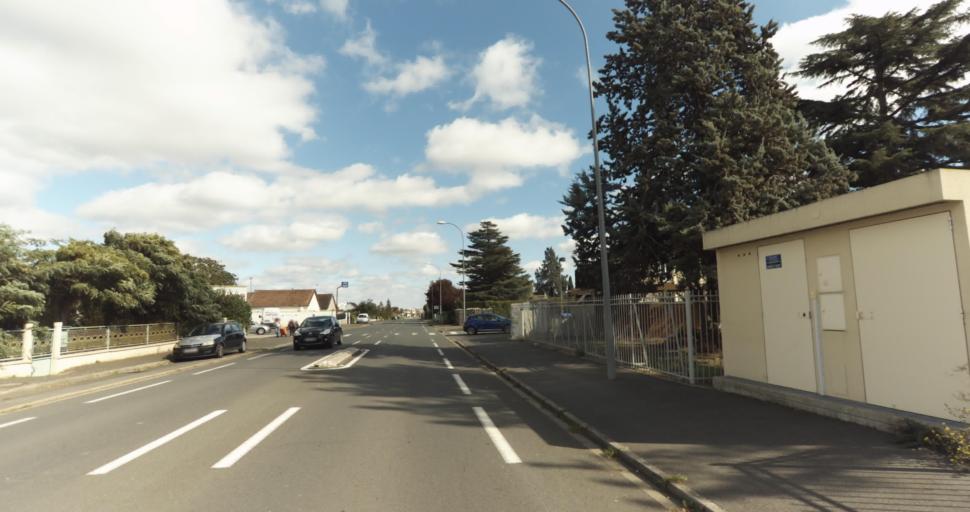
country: FR
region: Centre
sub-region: Departement d'Eure-et-Loir
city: Garnay
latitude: 48.7269
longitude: 1.3322
